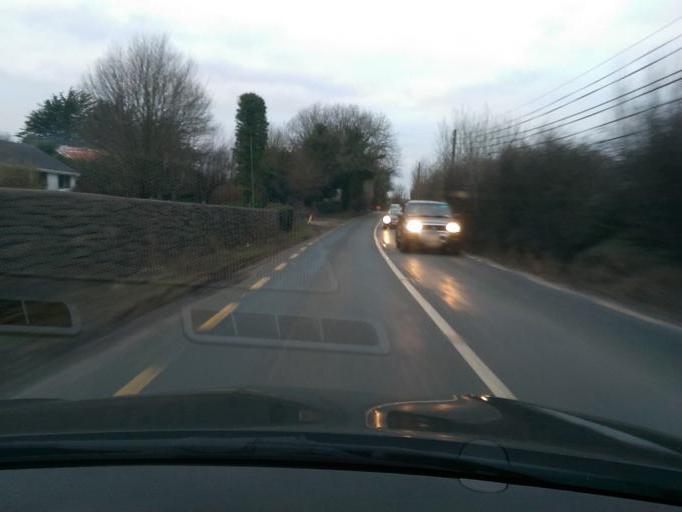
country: IE
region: Connaught
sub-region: County Galway
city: Moycullen
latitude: 53.3222
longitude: -9.1622
